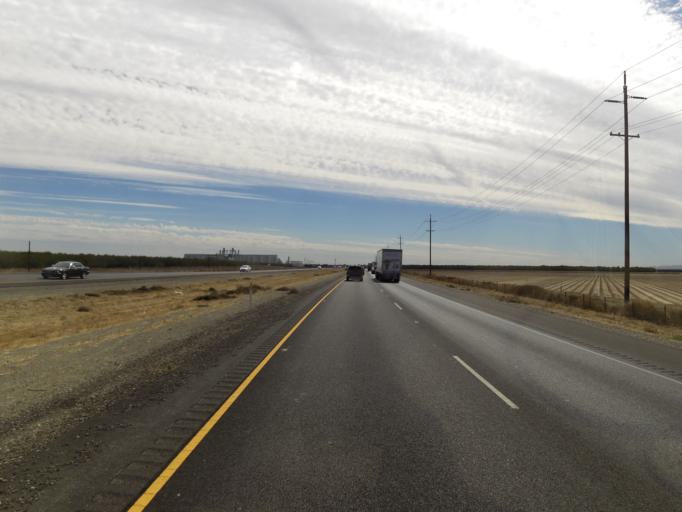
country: US
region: California
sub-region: Colusa County
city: Arbuckle
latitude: 39.0492
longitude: -122.0782
